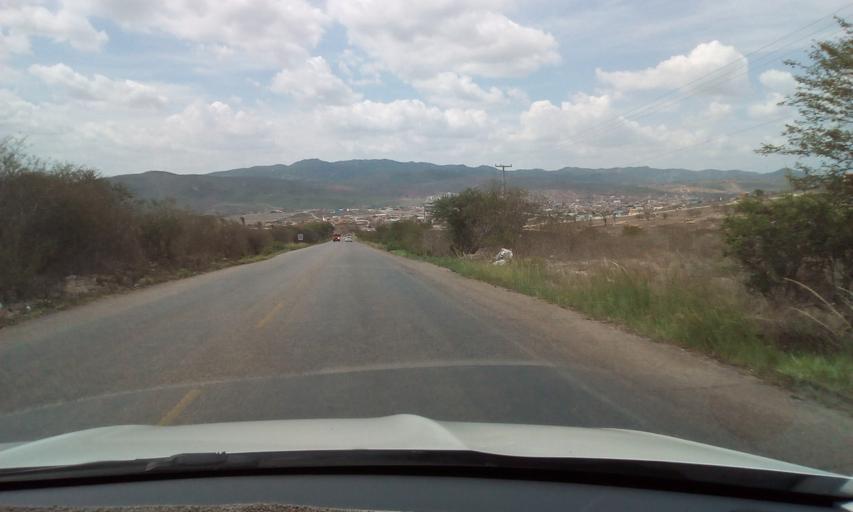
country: BR
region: Pernambuco
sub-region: Bezerros
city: Bezerros
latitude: -8.2636
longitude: -35.7551
